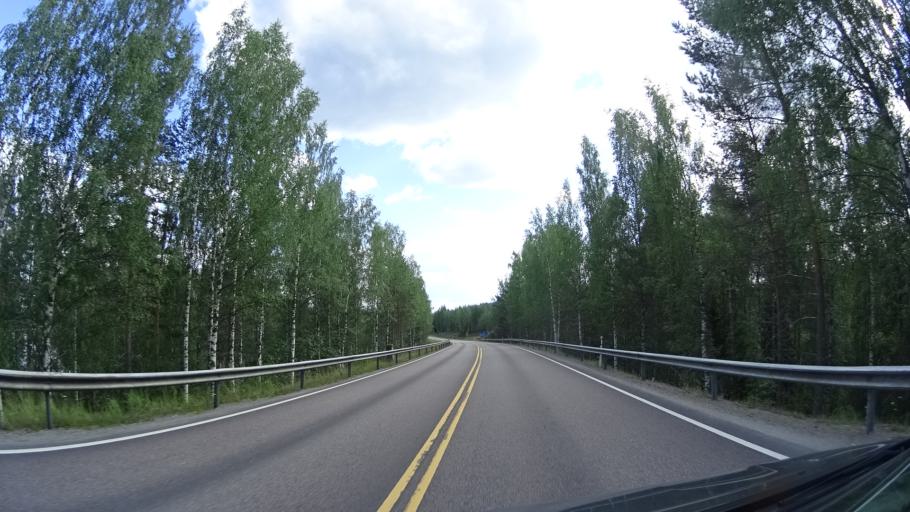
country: FI
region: Southern Savonia
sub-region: Savonlinna
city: Punkaharju
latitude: 61.6790
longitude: 29.4134
